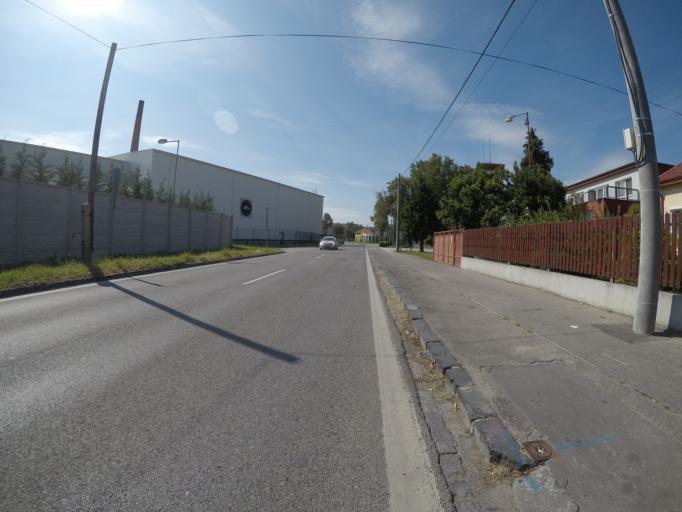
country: SK
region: Trnavsky
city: Dunajska Streda
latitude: 47.9976
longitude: 17.6237
